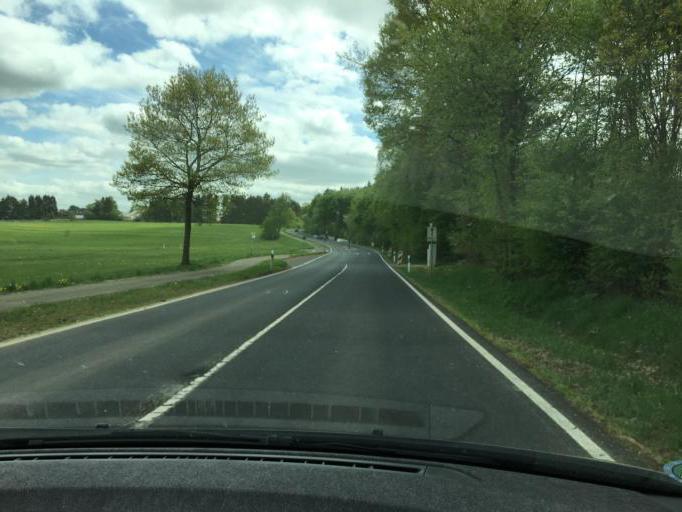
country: DE
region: Rheinland-Pfalz
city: Kirchsahr
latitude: 50.5269
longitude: 6.8550
